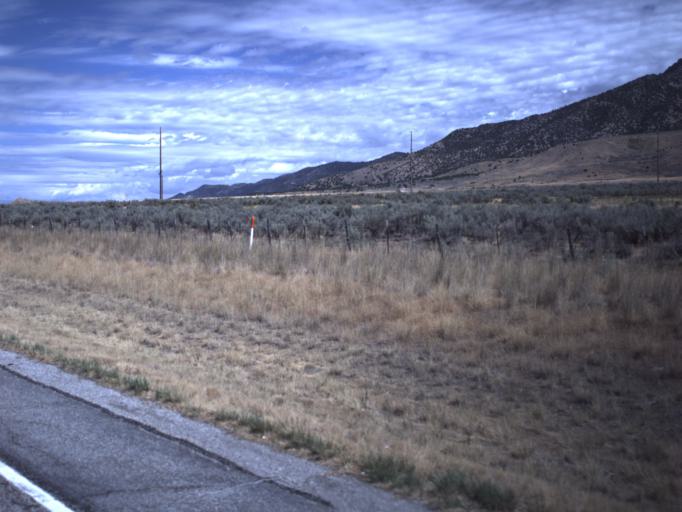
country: US
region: Utah
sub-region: Box Elder County
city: Garland
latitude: 41.8850
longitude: -112.1591
